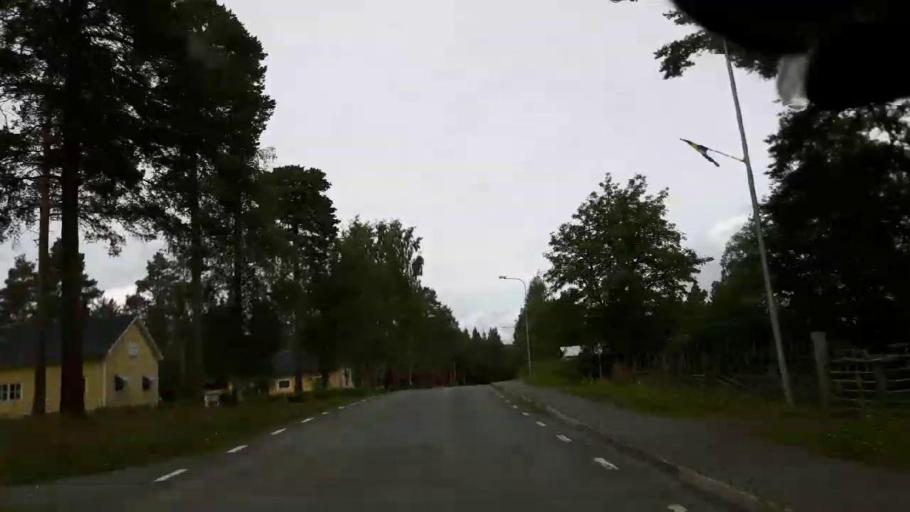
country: SE
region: Jaemtland
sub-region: Krokoms Kommun
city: Valla
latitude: 63.4600
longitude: 14.0621
